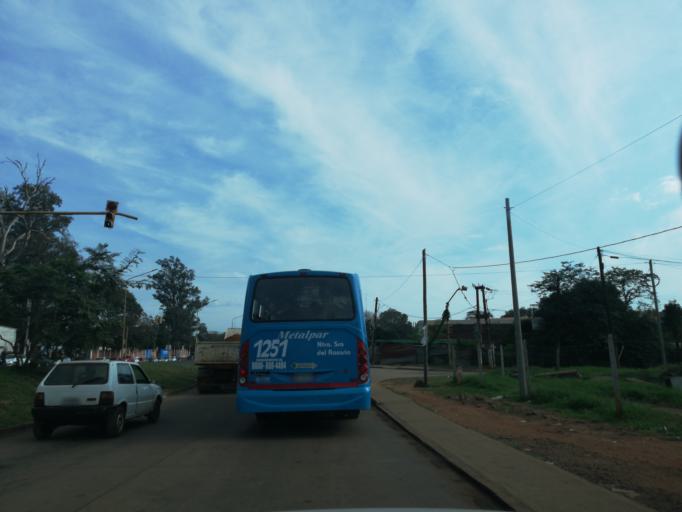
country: AR
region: Misiones
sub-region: Departamento de Capital
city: Posadas
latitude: -27.4270
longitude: -55.8938
